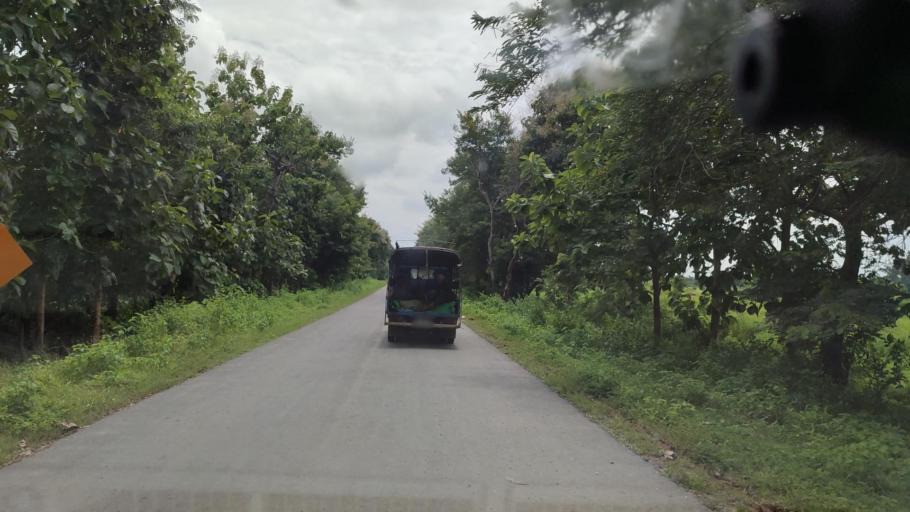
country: MM
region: Bago
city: Pyay
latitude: 18.8706
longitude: 95.2420
